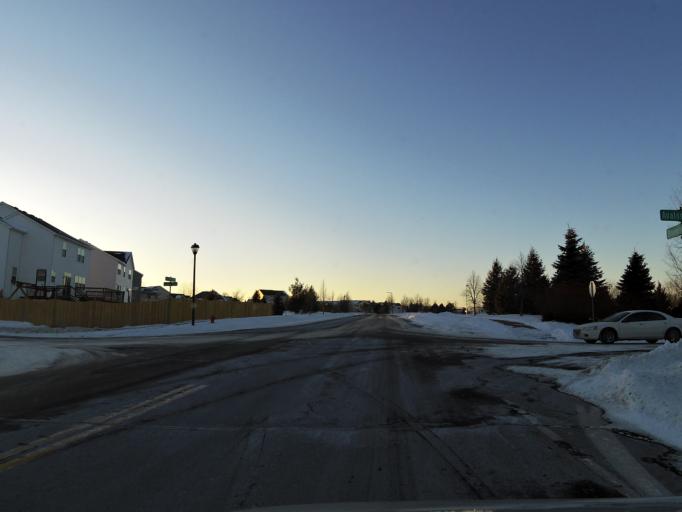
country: US
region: Minnesota
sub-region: Dakota County
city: Rosemount
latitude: 44.7424
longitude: -93.1051
